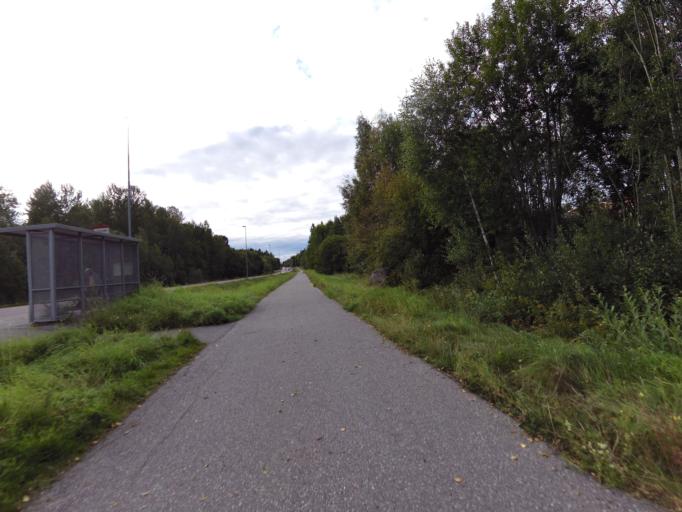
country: SE
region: Gaevleborg
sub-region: Gavle Kommun
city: Gavle
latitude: 60.6642
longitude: 17.1978
